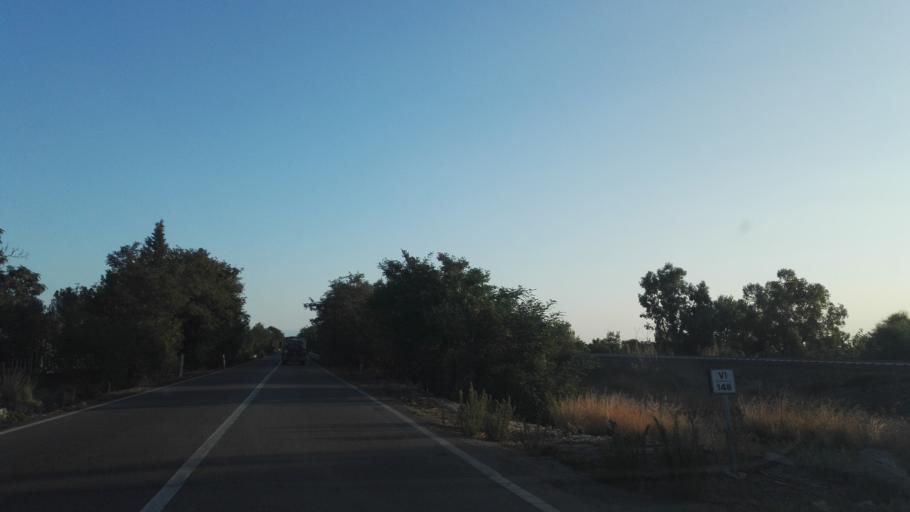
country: IT
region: Calabria
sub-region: Provincia di Catanzaro
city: Badolato Marina
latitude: 38.5534
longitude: 16.5705
